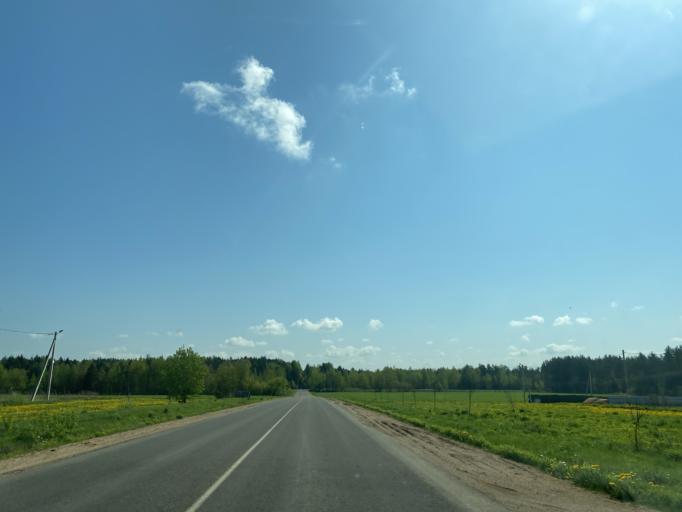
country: BY
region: Minsk
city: Horad Barysaw
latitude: 54.1792
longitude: 28.5646
